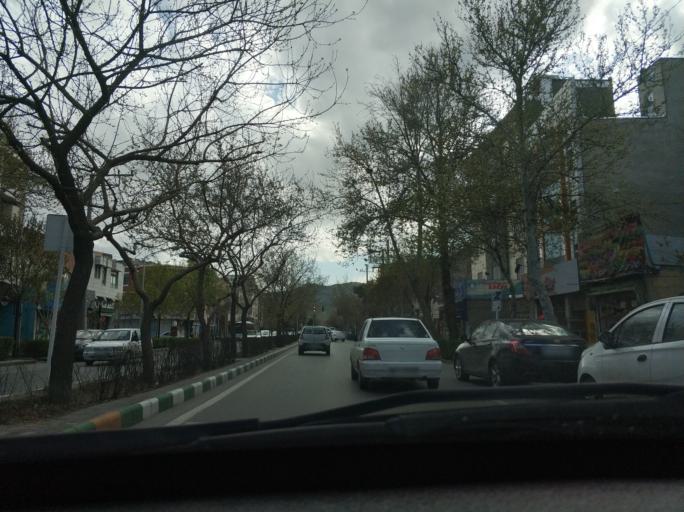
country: IR
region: Razavi Khorasan
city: Mashhad
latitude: 36.2722
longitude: 59.5902
